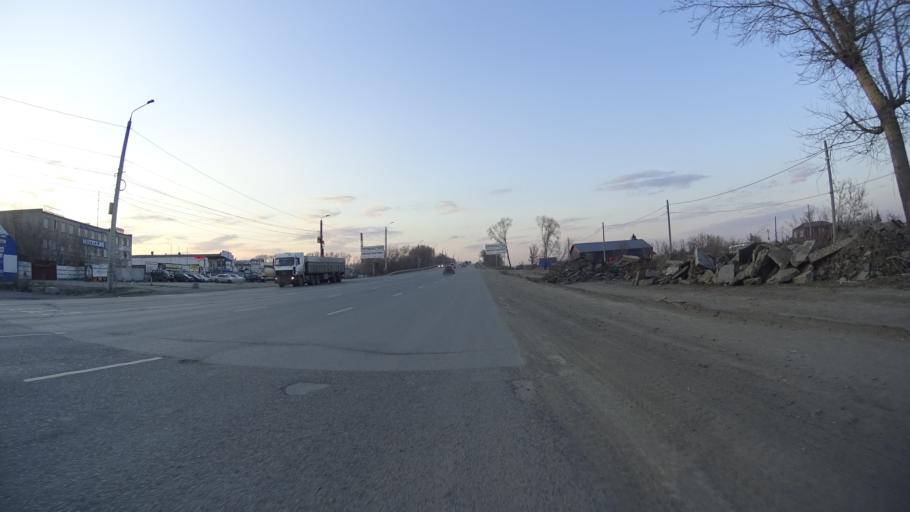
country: RU
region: Chelyabinsk
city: Novosineglazovskiy
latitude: 55.0979
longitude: 61.3879
